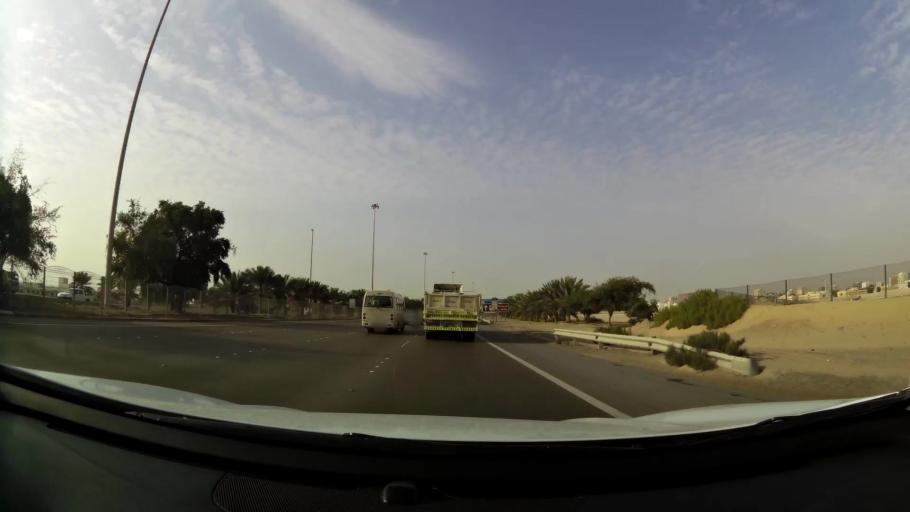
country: AE
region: Abu Dhabi
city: Abu Dhabi
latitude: 24.3131
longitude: 54.5271
